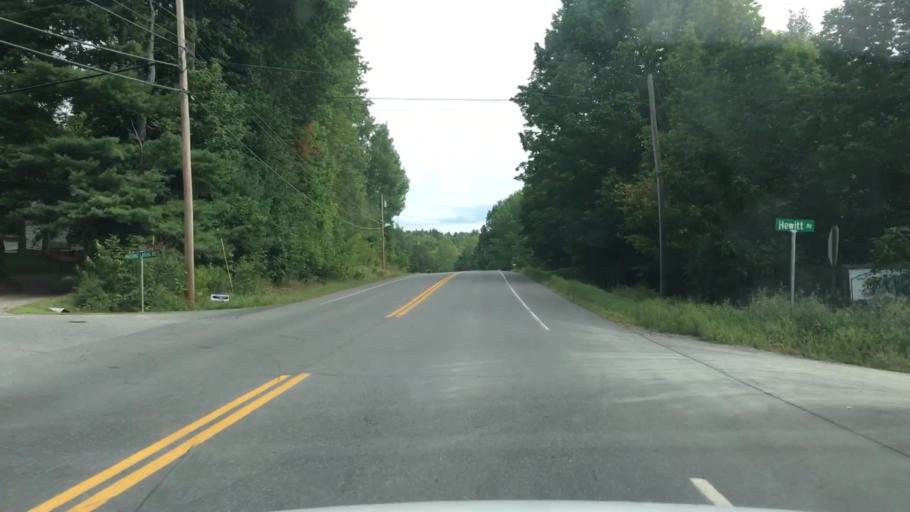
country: US
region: Maine
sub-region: Piscataquis County
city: Dover-Foxcroft
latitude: 45.2112
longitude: -69.1727
